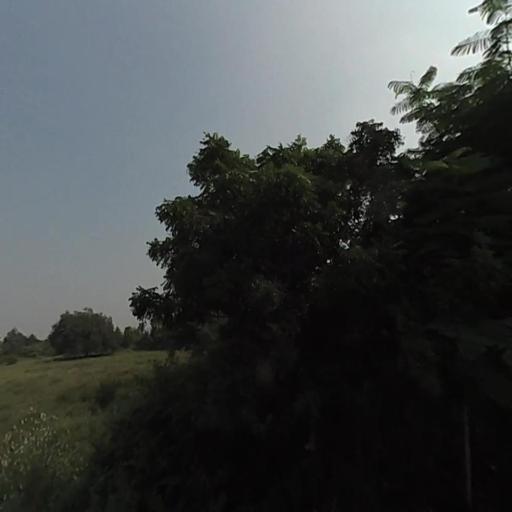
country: IN
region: Telangana
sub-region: Nalgonda
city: Nalgonda
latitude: 17.2045
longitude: 79.1461
